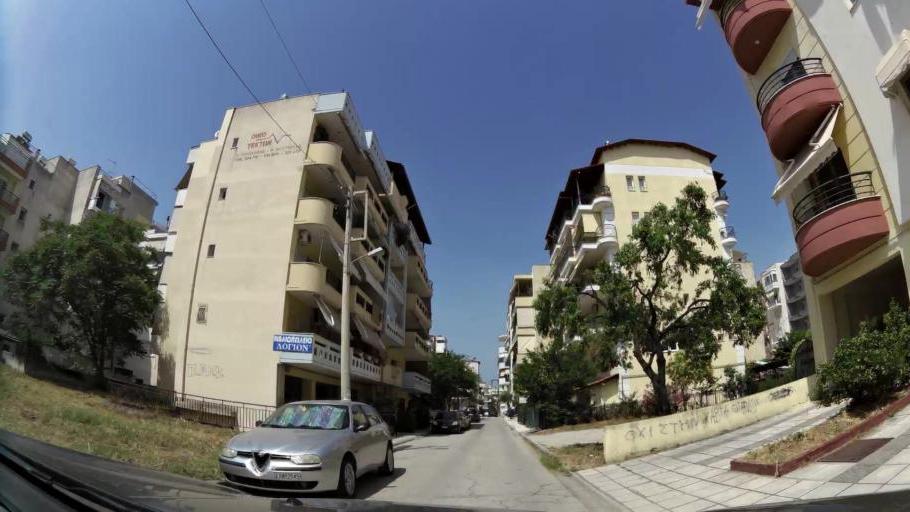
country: GR
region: Central Macedonia
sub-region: Nomos Thessalonikis
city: Evosmos
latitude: 40.6707
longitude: 22.9179
